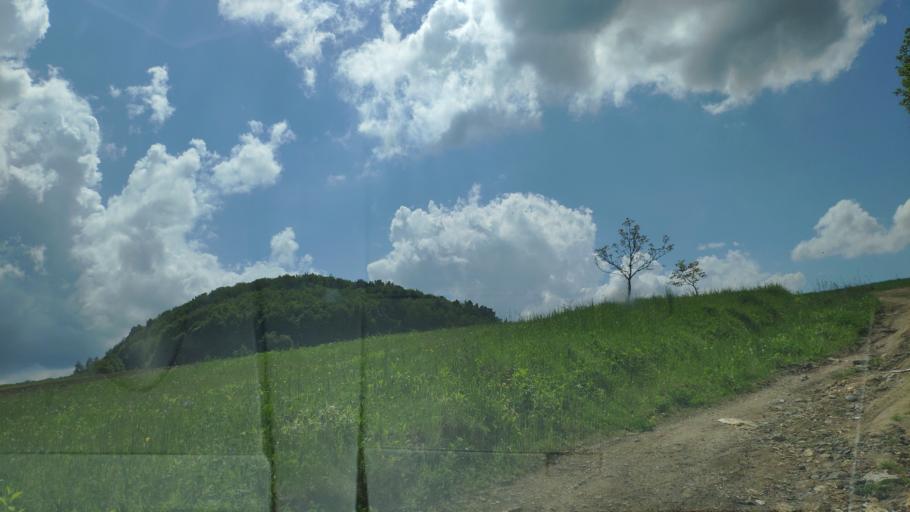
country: SK
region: Presovsky
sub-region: Okres Presov
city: Presov
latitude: 48.9510
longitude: 21.1150
